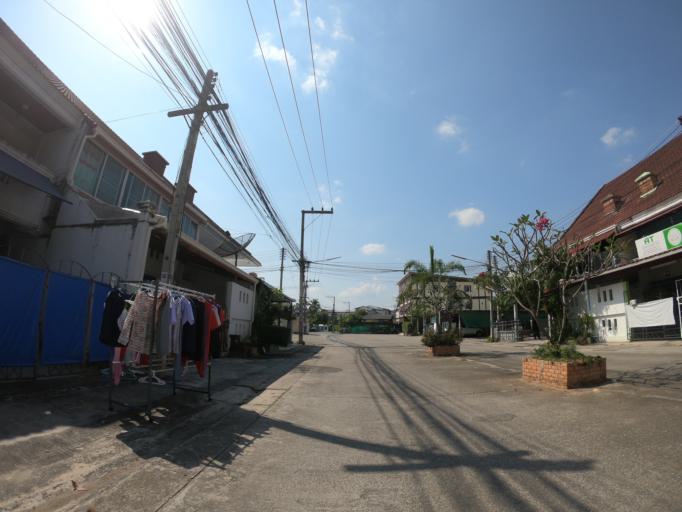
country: TH
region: Chiang Mai
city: Chiang Mai
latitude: 18.8119
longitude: 99.0152
